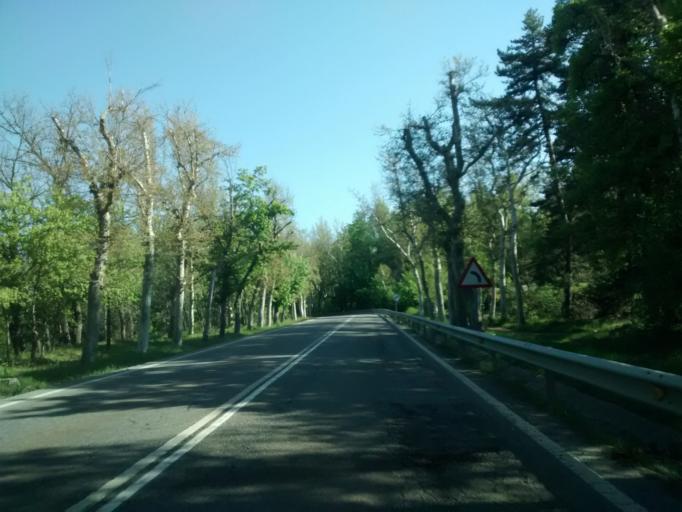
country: ES
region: Castille and Leon
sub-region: Provincia de Segovia
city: San Ildefonso
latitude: 40.8941
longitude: -4.0120
